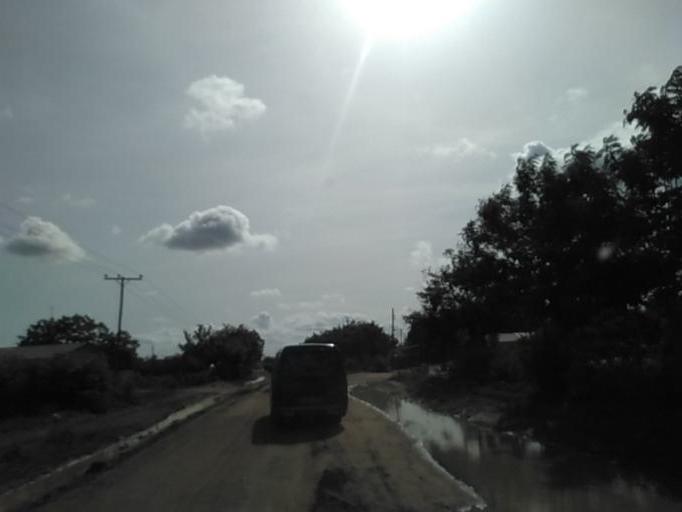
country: GH
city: Akropong
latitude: 6.0319
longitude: 0.3401
